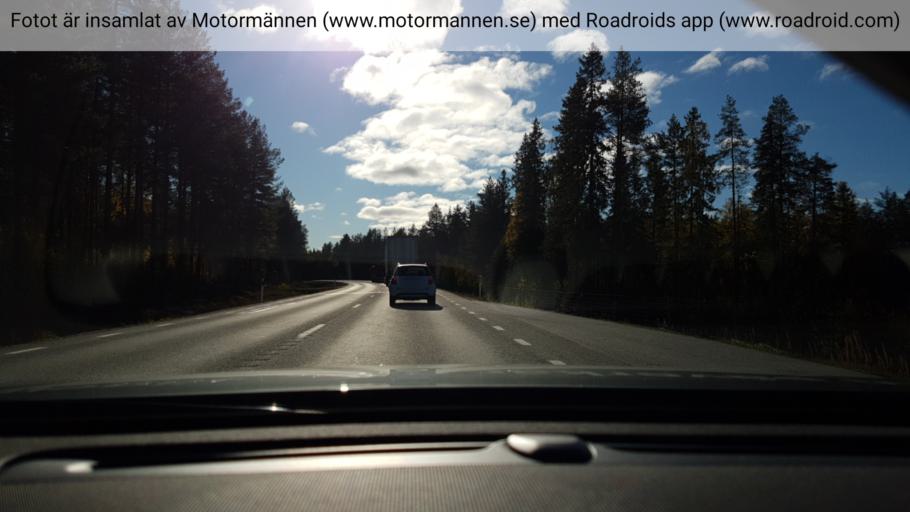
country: SE
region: Vaesterbotten
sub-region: Skelleftea Kommun
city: Burea
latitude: 64.4916
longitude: 21.2710
